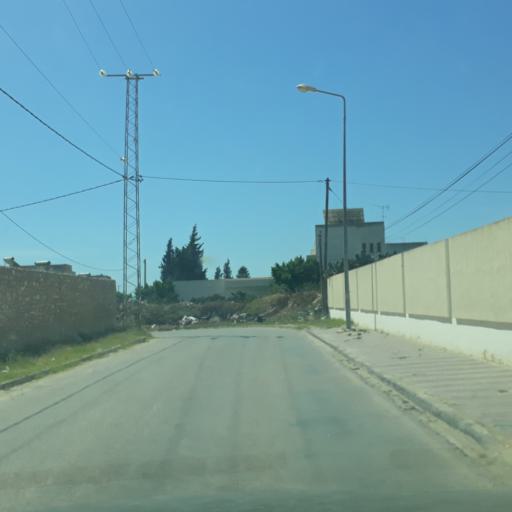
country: TN
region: Safaqis
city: Al Qarmadah
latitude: 34.7978
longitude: 10.7570
